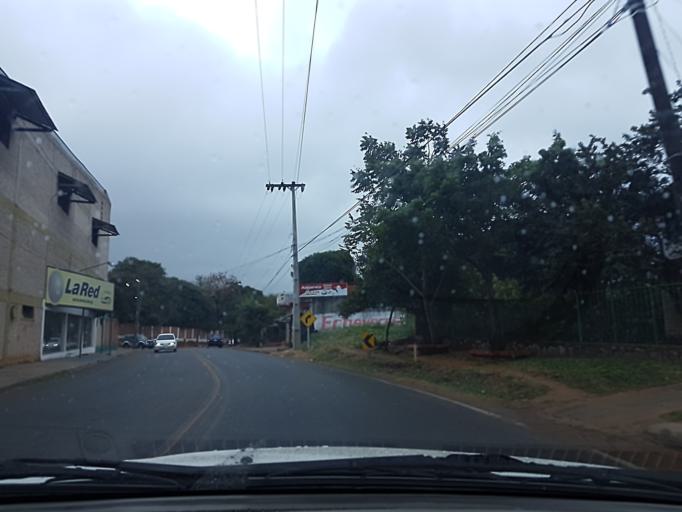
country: PY
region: Central
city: San Lorenzo
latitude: -25.2536
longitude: -57.5007
